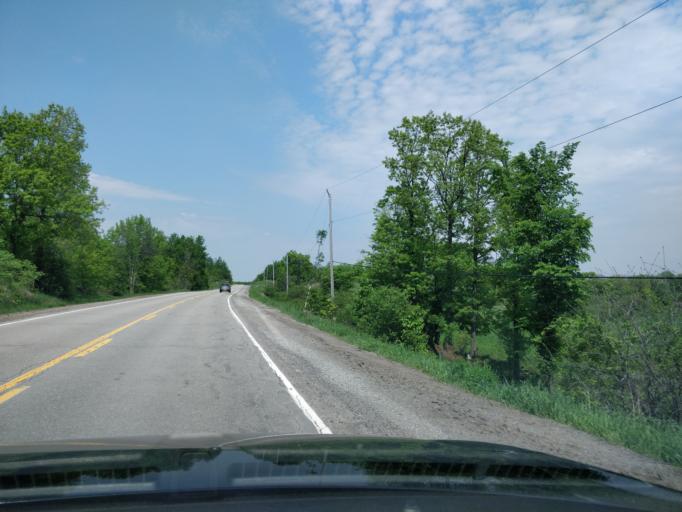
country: CA
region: Ontario
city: Perth
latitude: 44.7324
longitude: -76.3964
